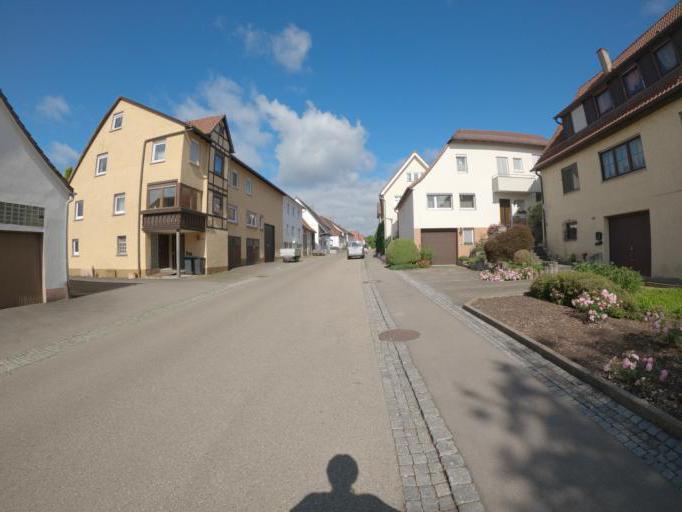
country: DE
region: Baden-Wuerttemberg
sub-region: Regierungsbezirk Stuttgart
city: Ebersbach an der Fils
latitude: 48.7260
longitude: 9.5491
